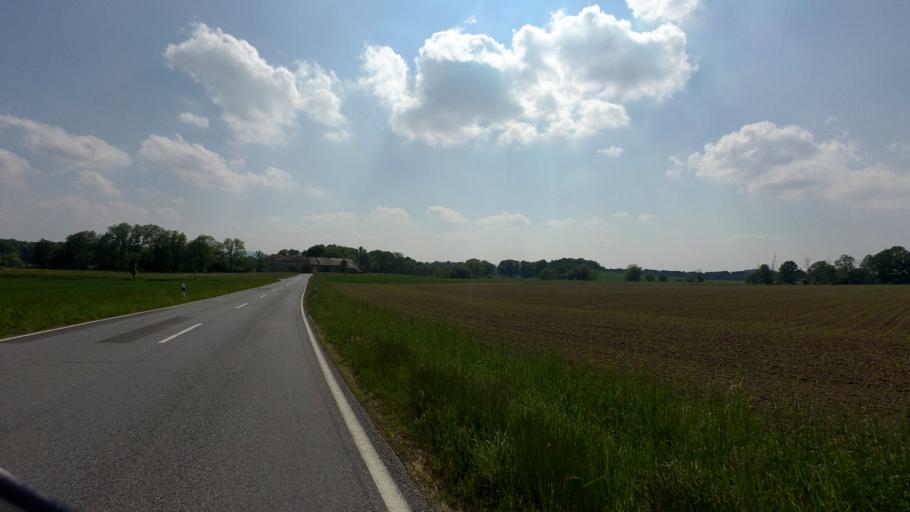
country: DE
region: Saxony
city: Weissenberg
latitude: 51.2027
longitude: 14.6040
